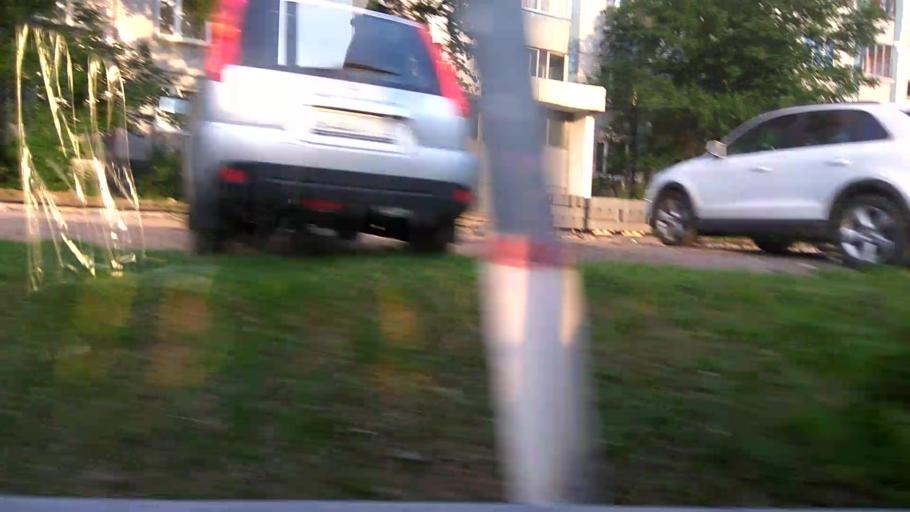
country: RU
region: Moskovskaya
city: Yubileyny
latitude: 55.9236
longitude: 37.8563
